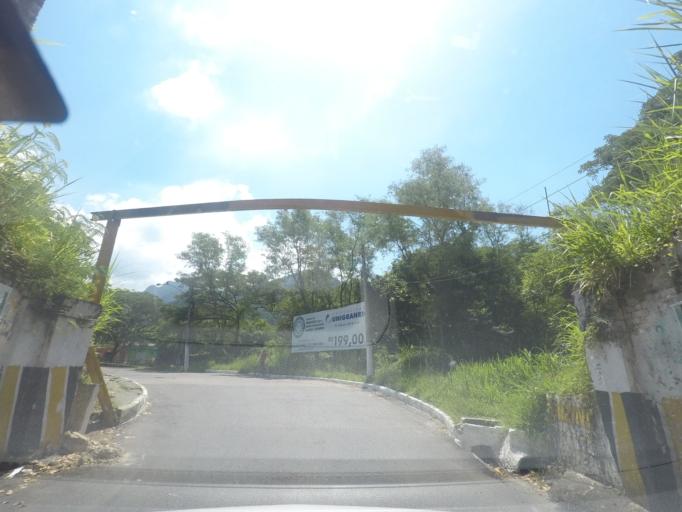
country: BR
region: Rio de Janeiro
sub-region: Petropolis
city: Petropolis
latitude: -22.5762
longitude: -43.1856
